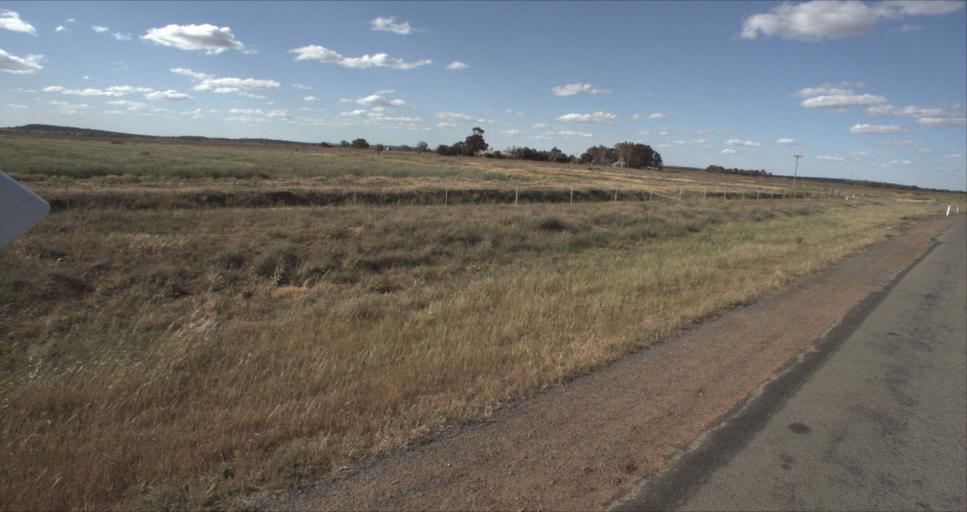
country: AU
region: New South Wales
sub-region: Leeton
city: Leeton
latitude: -34.4556
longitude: 146.2742
